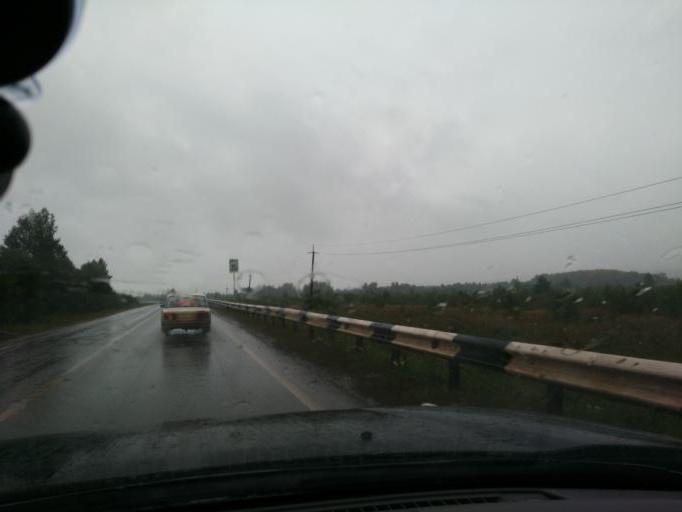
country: RU
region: Perm
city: Osa
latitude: 57.1714
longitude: 55.5320
